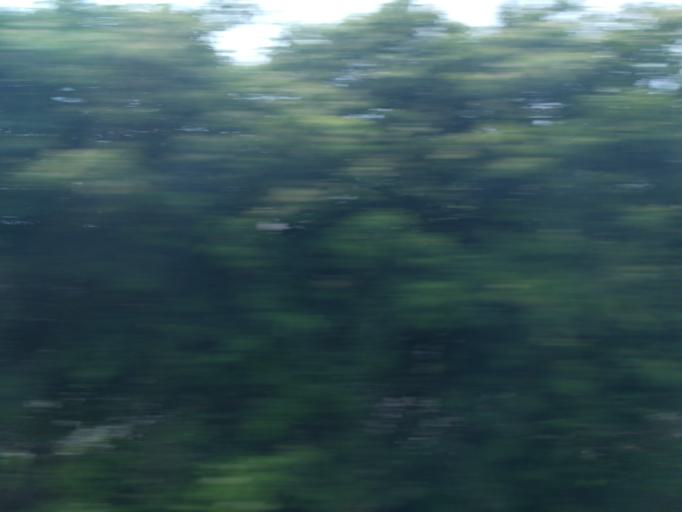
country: IT
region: Veneto
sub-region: Provincia di Vicenza
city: Monticello Conte Otto
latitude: 45.5847
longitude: 11.5691
